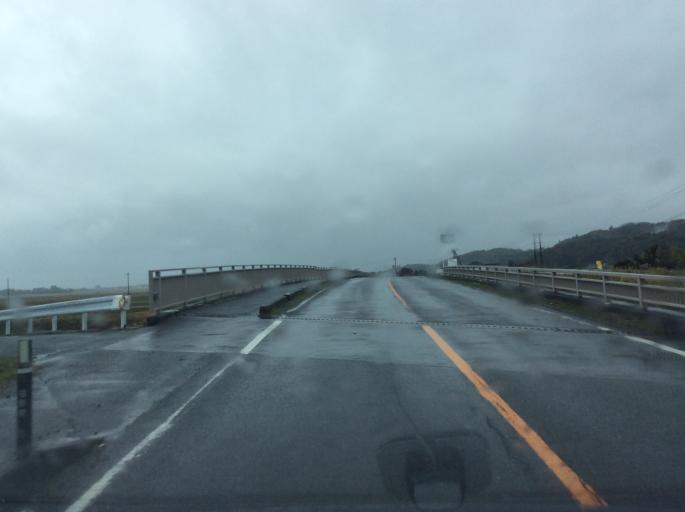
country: JP
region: Fukushima
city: Iwaki
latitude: 37.1122
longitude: 140.9530
